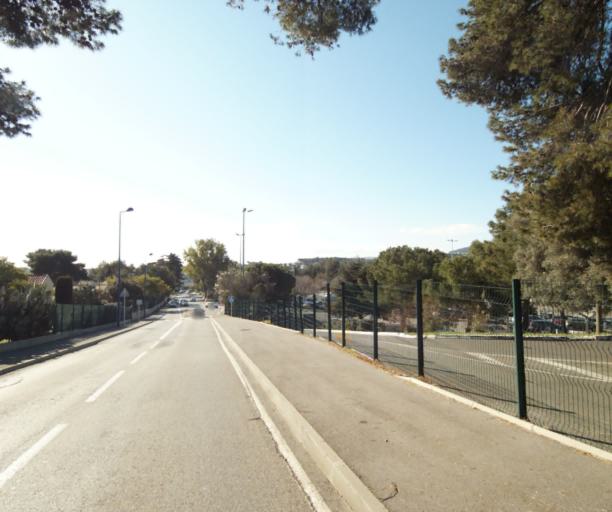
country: FR
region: Provence-Alpes-Cote d'Azur
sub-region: Departement des Alpes-Maritimes
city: Biot
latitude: 43.6042
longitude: 7.0921
